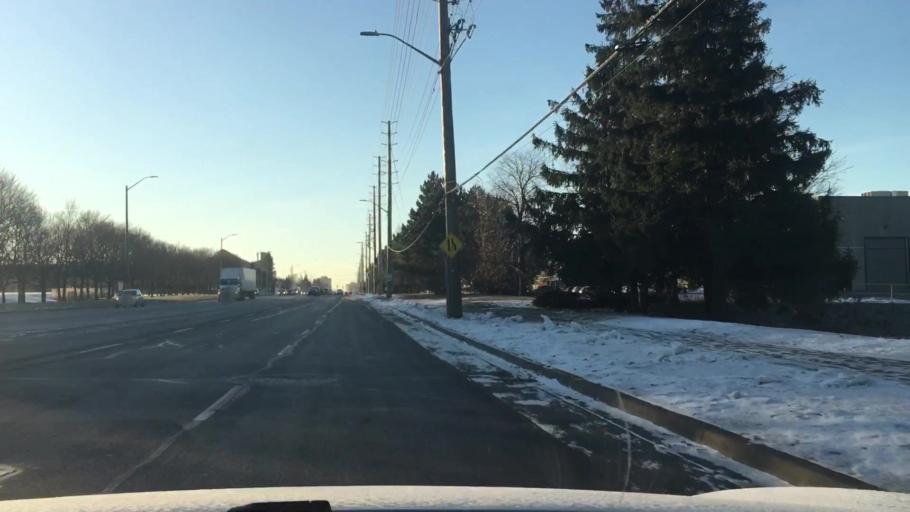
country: CA
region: Ontario
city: Markham
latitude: 43.8327
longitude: -79.3280
